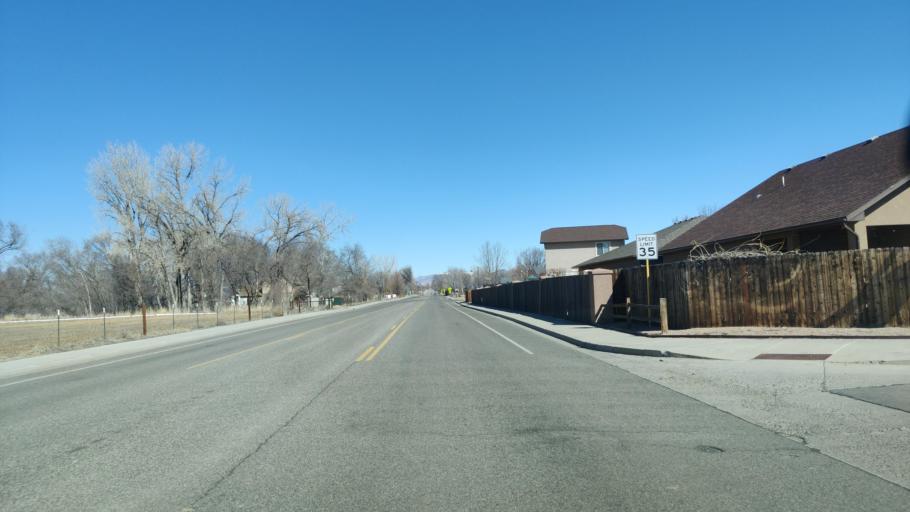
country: US
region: Colorado
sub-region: Mesa County
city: Fruita
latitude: 39.1653
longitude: -108.7197
